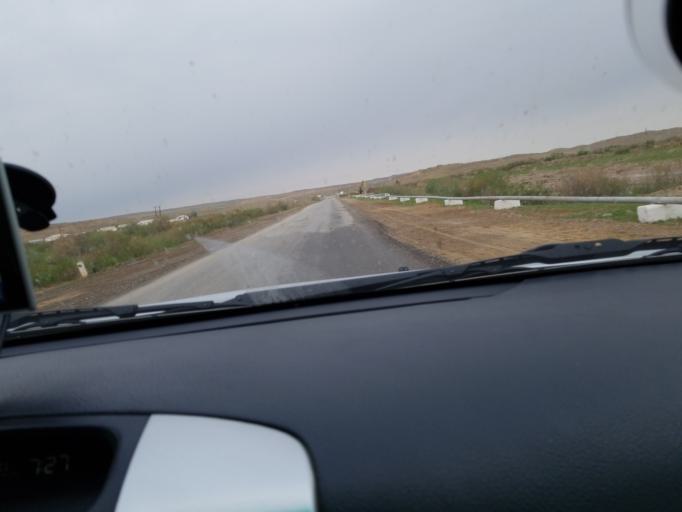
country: AF
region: Badghis
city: Bala Murghab
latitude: 35.9651
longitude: 62.7352
